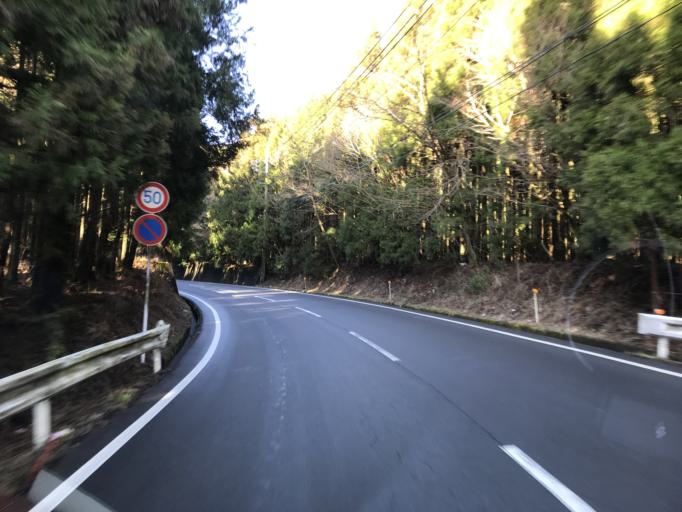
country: JP
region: Shizuoka
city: Gotemba
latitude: 35.2608
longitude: 138.8288
